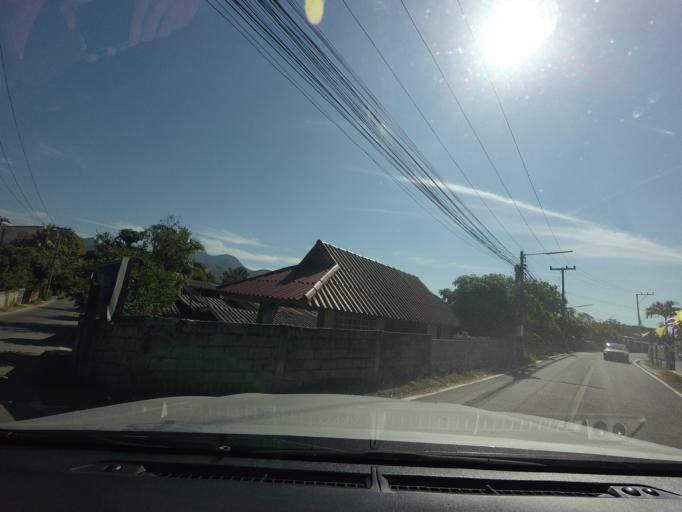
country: TH
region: Mae Hong Son
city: Wiang Nuea
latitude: 19.3860
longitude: 98.4397
